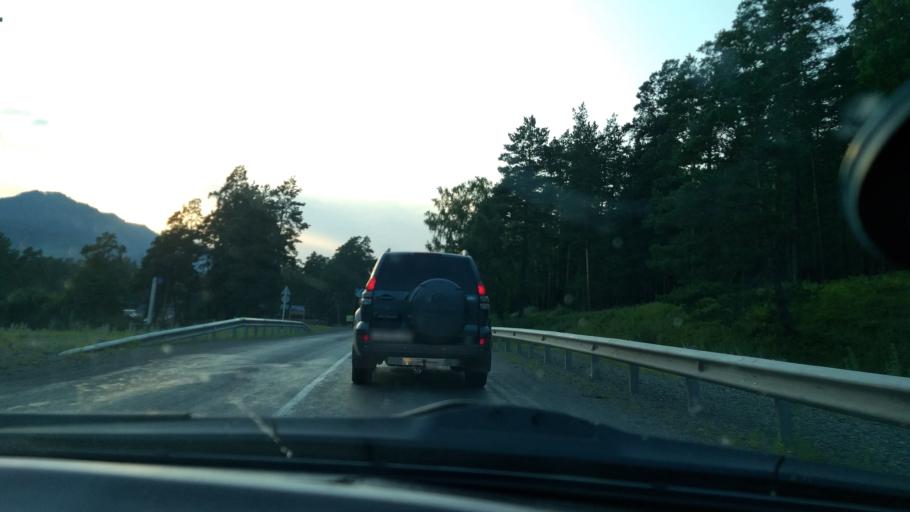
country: RU
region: Altay
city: Elekmonar
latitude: 51.5963
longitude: 85.8251
